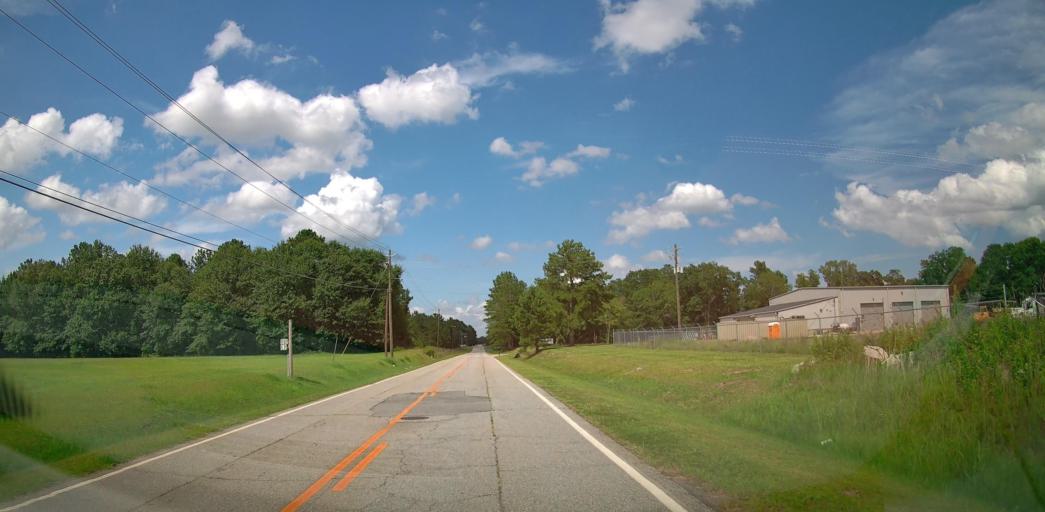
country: US
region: Georgia
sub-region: Houston County
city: Centerville
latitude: 32.6951
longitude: -83.6685
